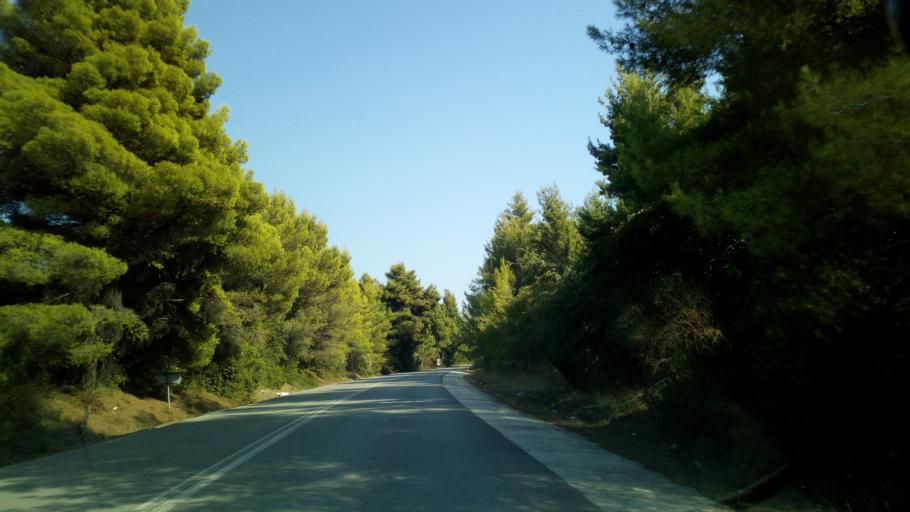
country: GR
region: Central Macedonia
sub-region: Nomos Chalkidikis
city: Pefkochori
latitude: 39.9745
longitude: 23.6666
